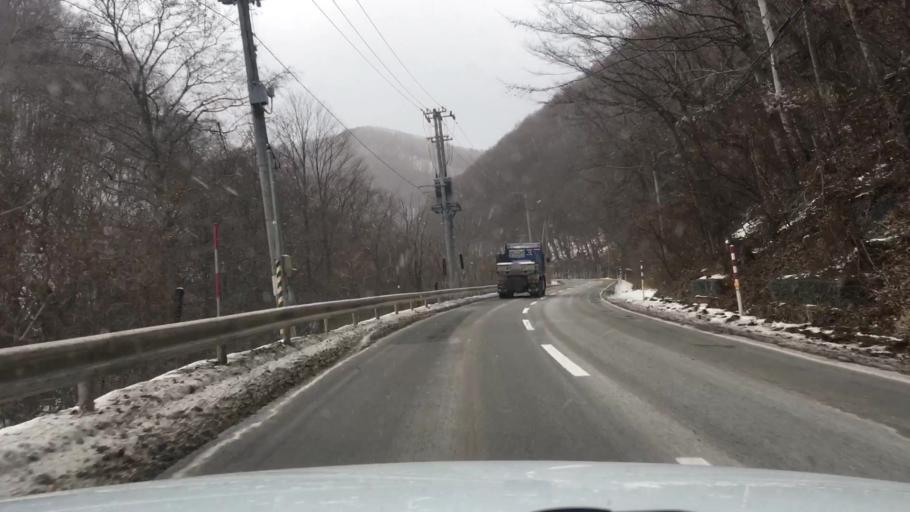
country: JP
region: Iwate
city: Tono
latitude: 39.6264
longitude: 141.4671
